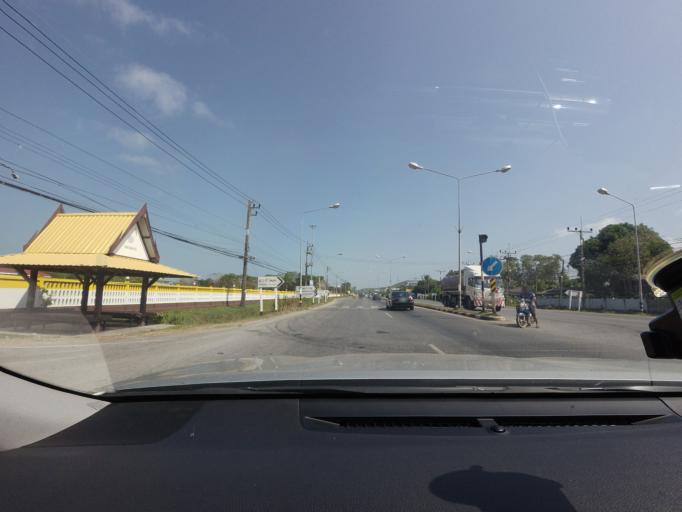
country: TH
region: Songkhla
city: Singhanakhon
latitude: 7.2376
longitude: 100.5512
